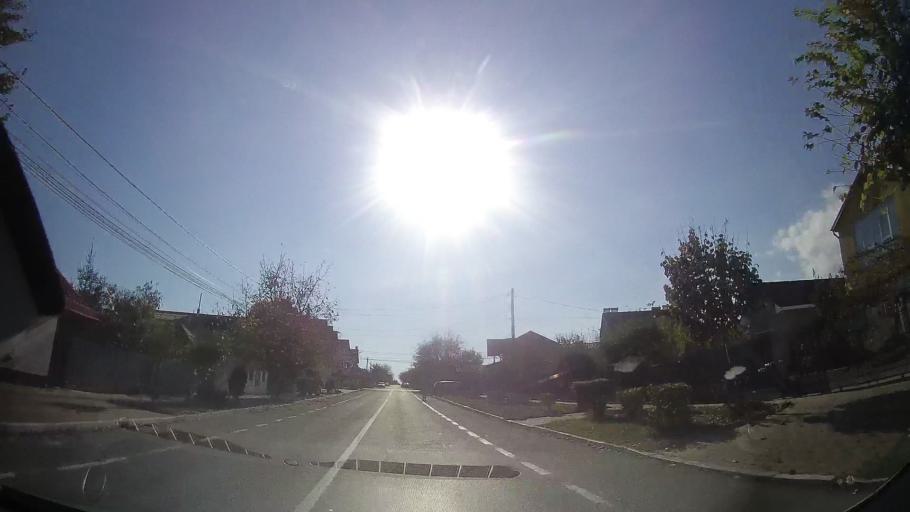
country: RO
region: Constanta
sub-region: Comuna Costinesti
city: Schitu
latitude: 43.9419
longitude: 28.6293
